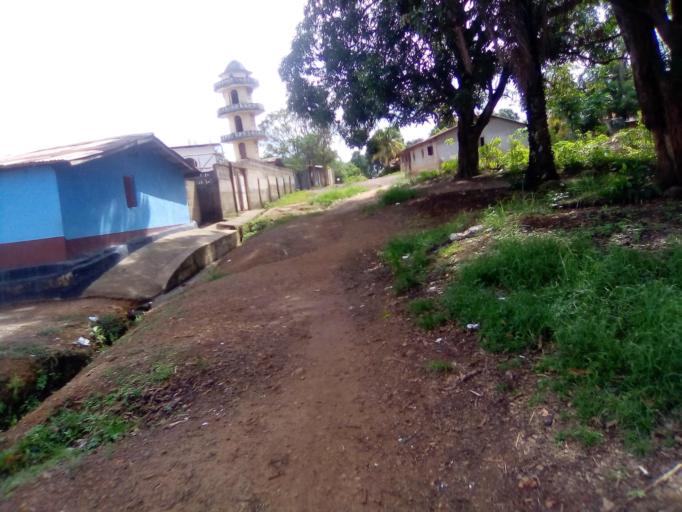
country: SL
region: Southern Province
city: Bo
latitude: 7.9774
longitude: -11.7278
